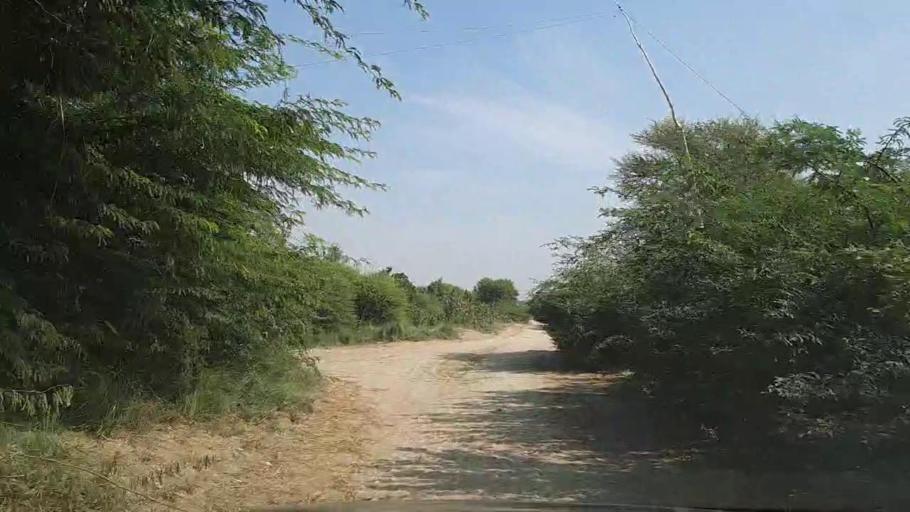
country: PK
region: Sindh
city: Thatta
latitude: 24.7991
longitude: 67.8542
